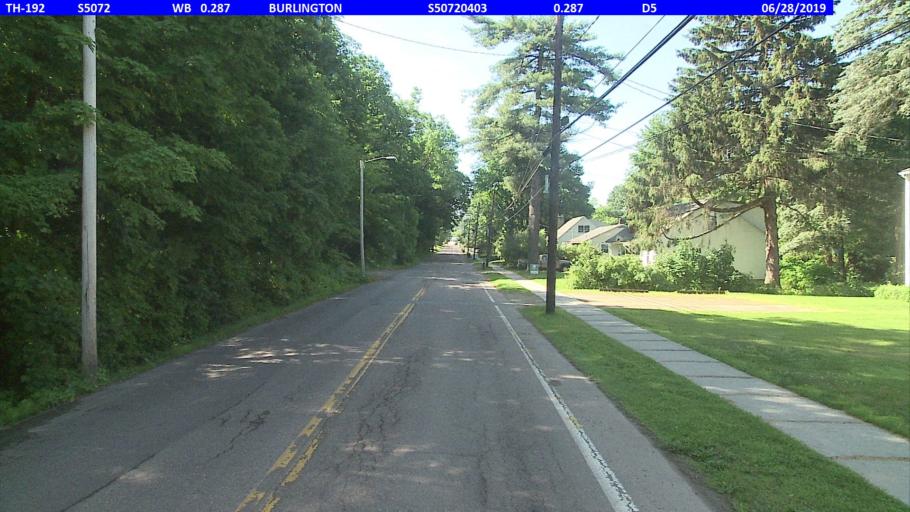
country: US
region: Vermont
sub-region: Chittenden County
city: Burlington
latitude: 44.5078
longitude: -73.2413
